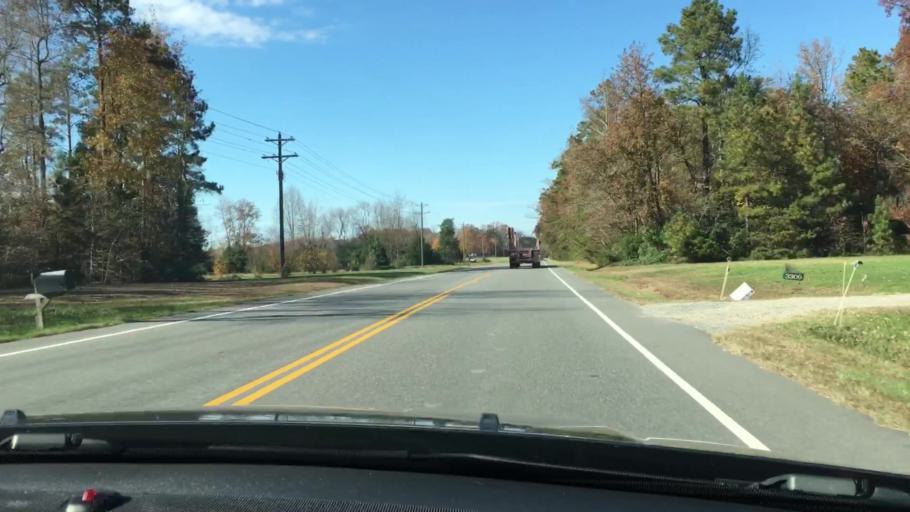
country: US
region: Virginia
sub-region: Hanover County
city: Hanover
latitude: 37.8011
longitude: -77.2614
